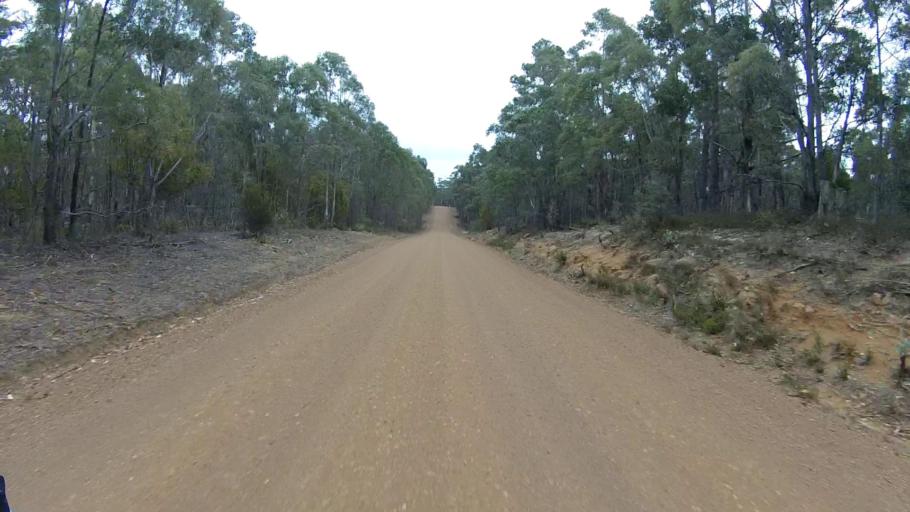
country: AU
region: Tasmania
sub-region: Sorell
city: Sorell
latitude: -42.5885
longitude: 147.8855
